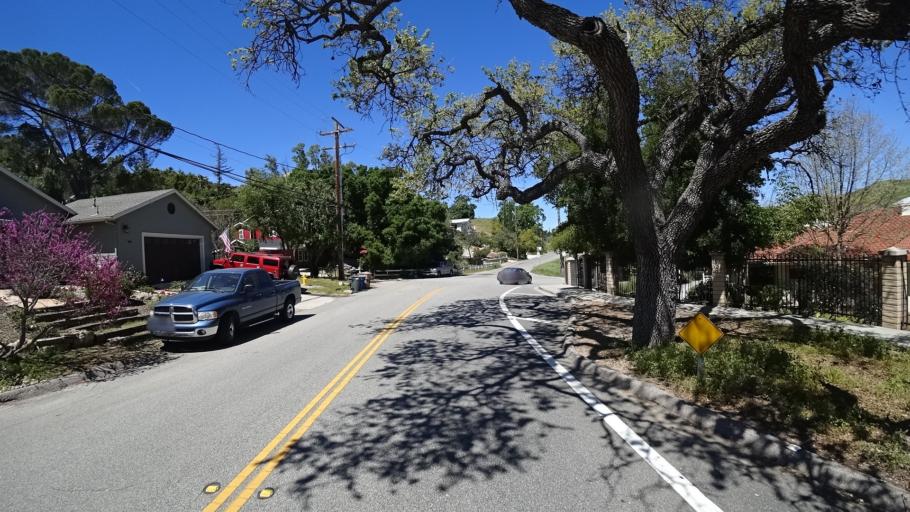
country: US
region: California
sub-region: Ventura County
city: Thousand Oaks
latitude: 34.1648
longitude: -118.8406
